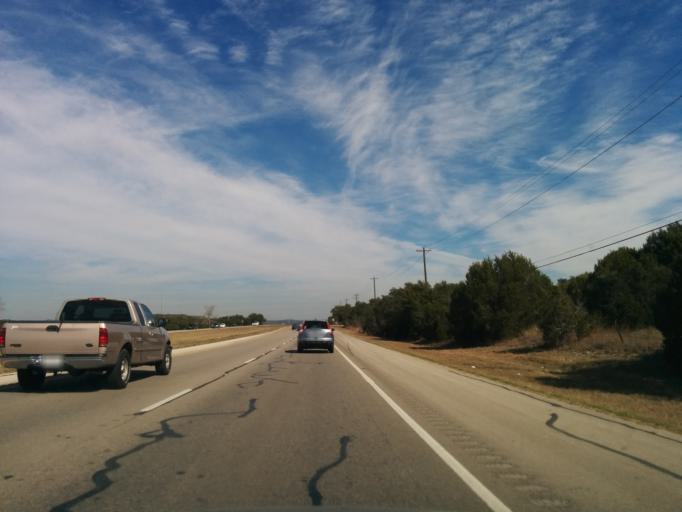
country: US
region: Texas
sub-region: Comal County
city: Bulverde
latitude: 29.8201
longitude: -98.4178
